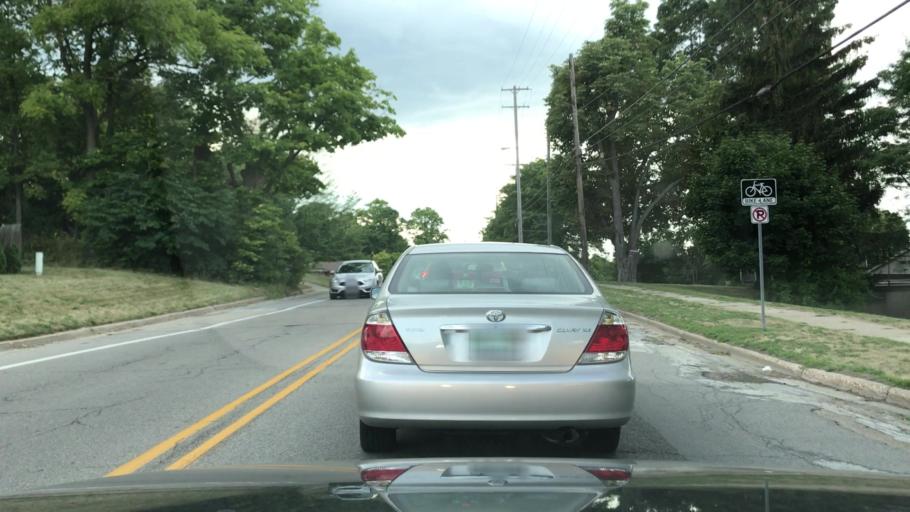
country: US
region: Michigan
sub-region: Kent County
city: Grand Rapids
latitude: 42.9990
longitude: -85.6414
